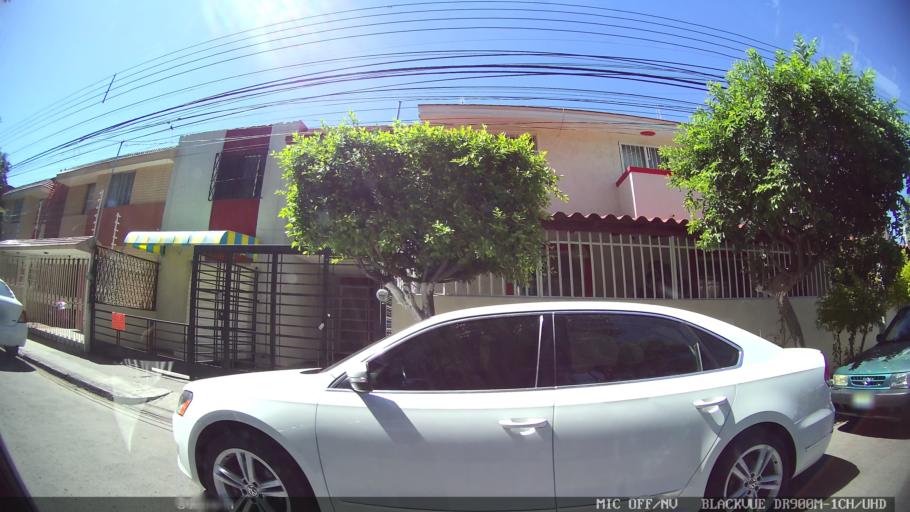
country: MX
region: Jalisco
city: Tlaquepaque
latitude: 20.6452
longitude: -103.2970
